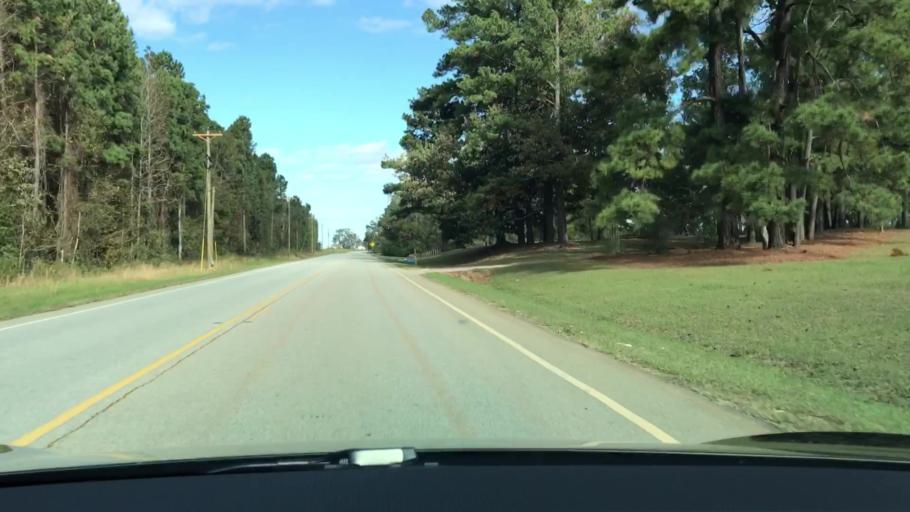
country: US
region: Georgia
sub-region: Jefferson County
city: Wrens
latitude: 33.1362
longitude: -82.4545
